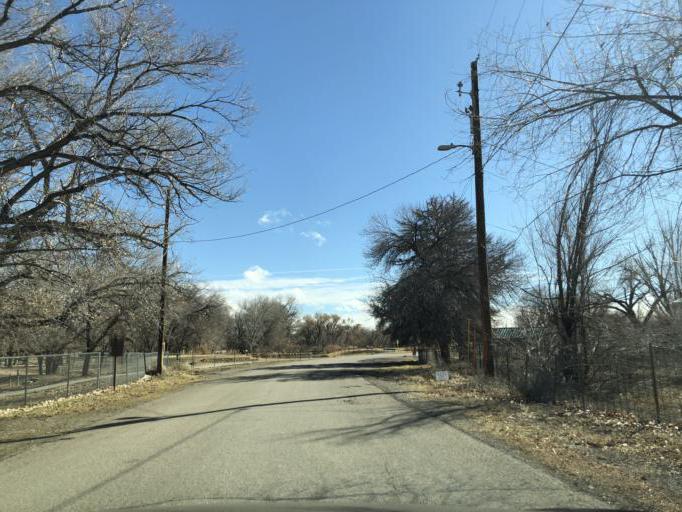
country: US
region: Utah
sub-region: Carbon County
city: East Carbon City
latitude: 38.9894
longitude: -110.1543
